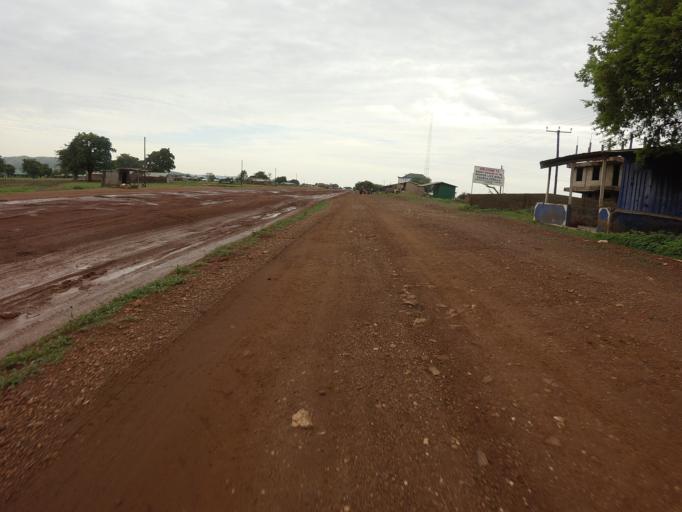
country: GH
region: Upper East
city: Bawku
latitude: 10.9282
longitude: -0.5041
